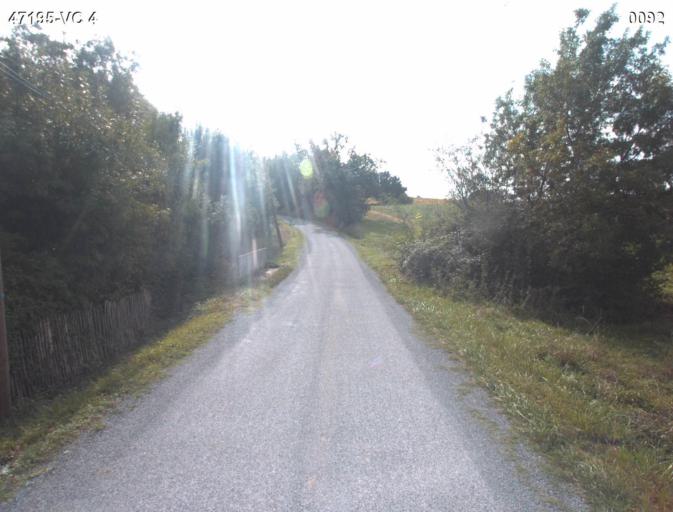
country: FR
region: Aquitaine
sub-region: Departement du Lot-et-Garonne
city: Nerac
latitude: 44.1198
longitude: 0.3757
